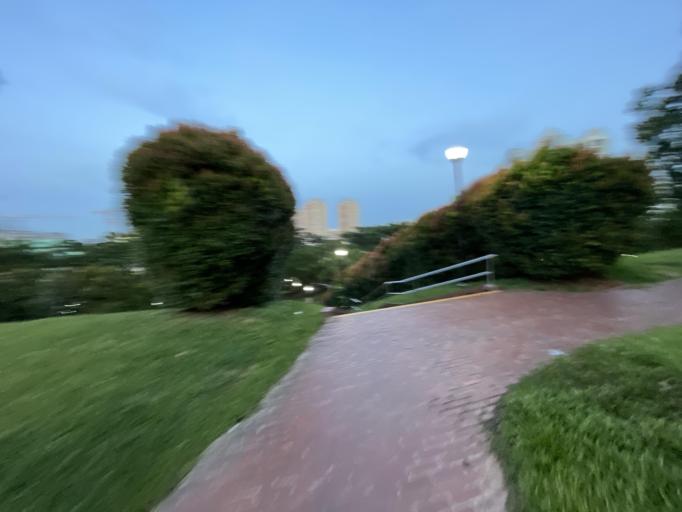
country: SG
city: Singapore
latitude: 1.3018
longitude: 103.7668
